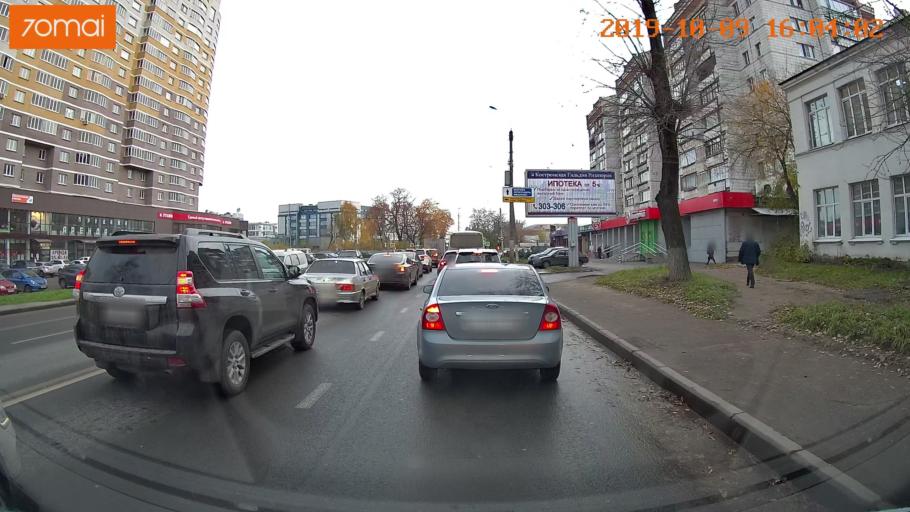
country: RU
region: Kostroma
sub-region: Kostromskoy Rayon
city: Kostroma
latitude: 57.7647
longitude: 40.9512
